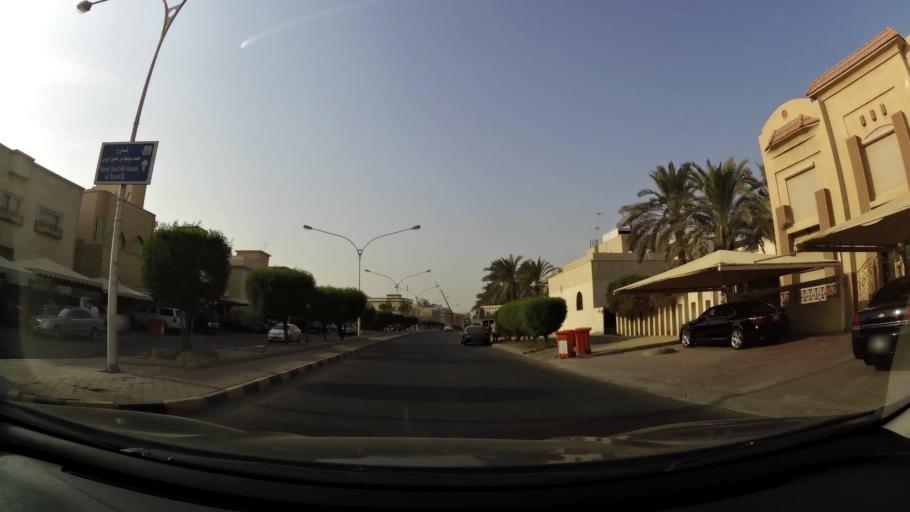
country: KW
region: Muhafazat Hawalli
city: Hawalli
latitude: 29.3164
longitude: 48.0024
